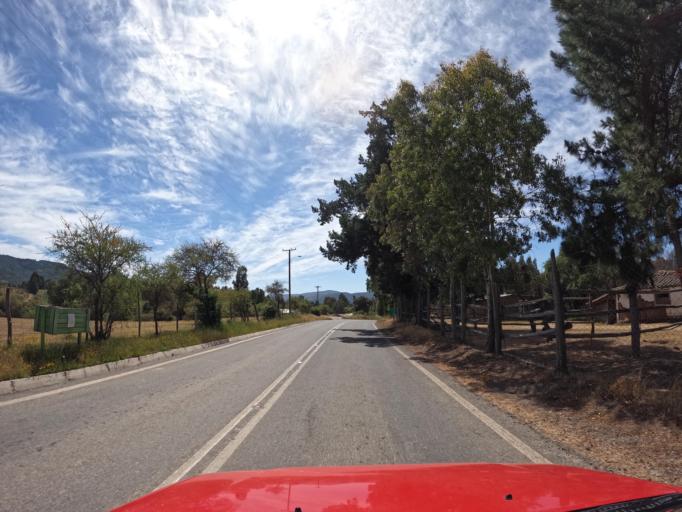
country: CL
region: Maule
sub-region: Provincia de Talca
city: Talca
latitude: -35.0100
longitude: -71.7856
